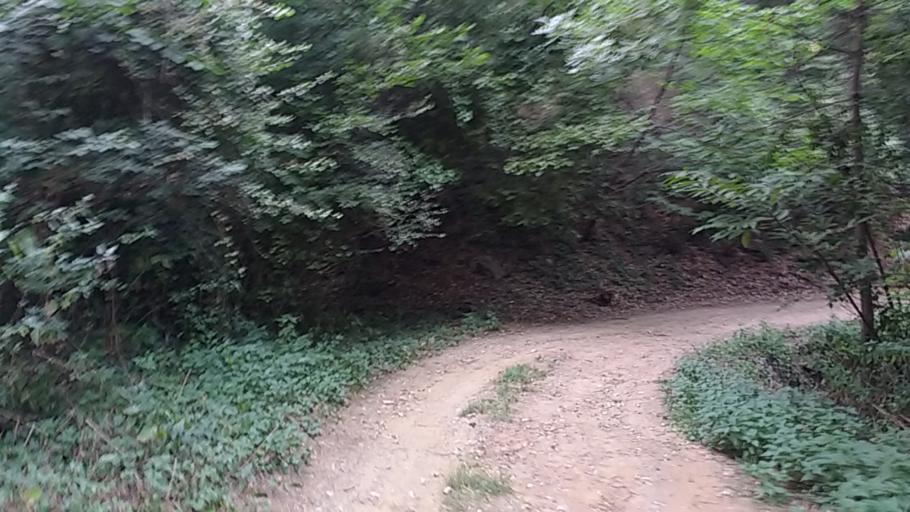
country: FR
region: Languedoc-Roussillon
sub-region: Departement des Pyrenees-Orientales
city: Ria-Sirach
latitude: 42.5932
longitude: 2.4157
